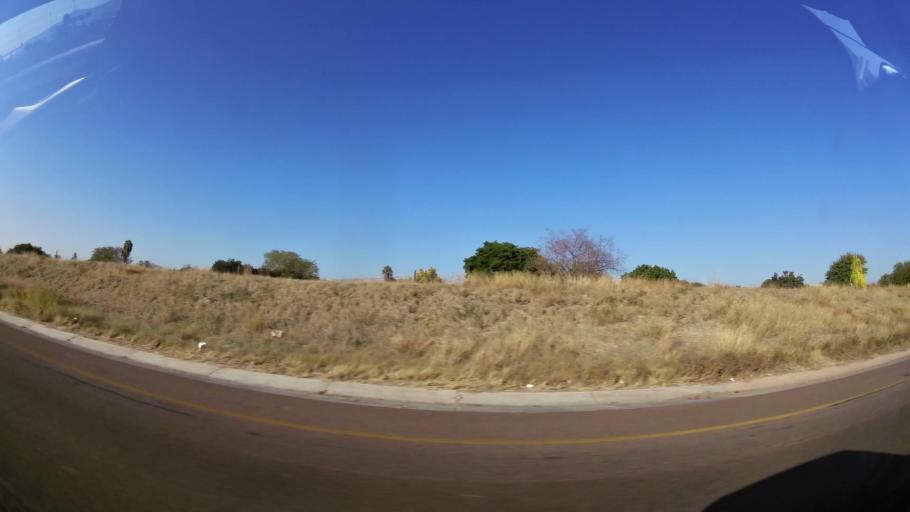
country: ZA
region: Gauteng
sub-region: City of Tshwane Metropolitan Municipality
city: Pretoria
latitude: -25.6433
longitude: 28.2408
